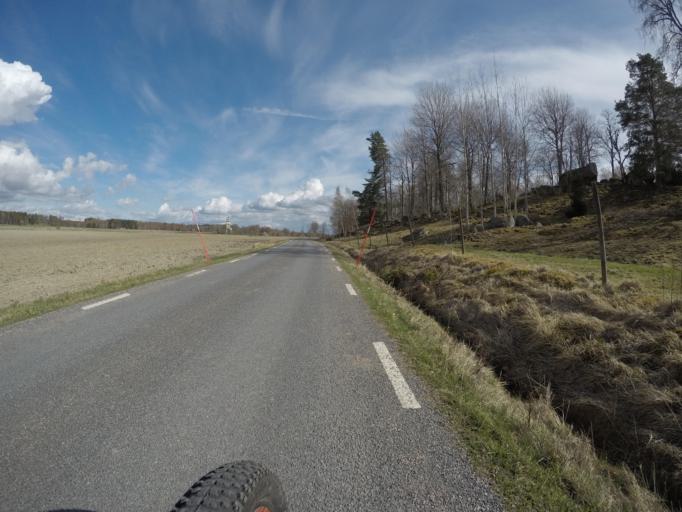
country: SE
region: Vaestmanland
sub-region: Kungsors Kommun
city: Kungsoer
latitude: 59.2878
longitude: 16.1483
